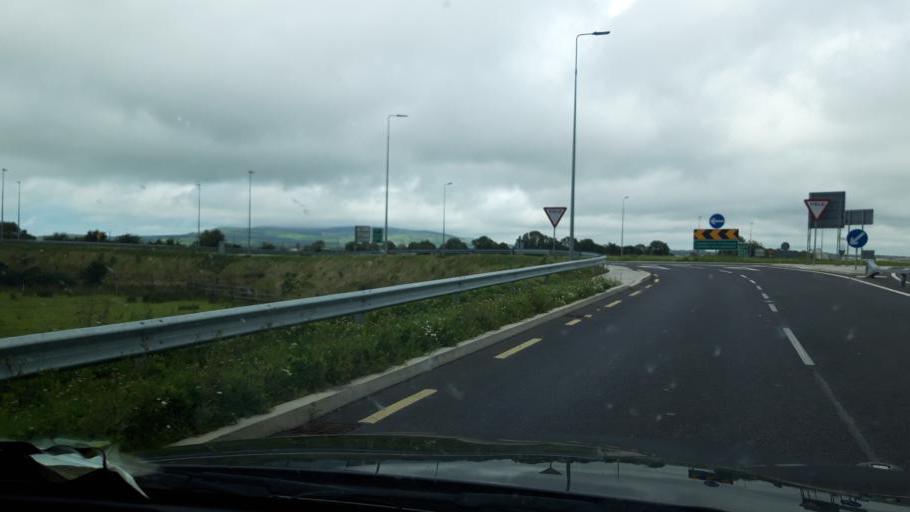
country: IE
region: Leinster
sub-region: Loch Garman
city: New Ross
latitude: 52.4178
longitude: -6.8613
